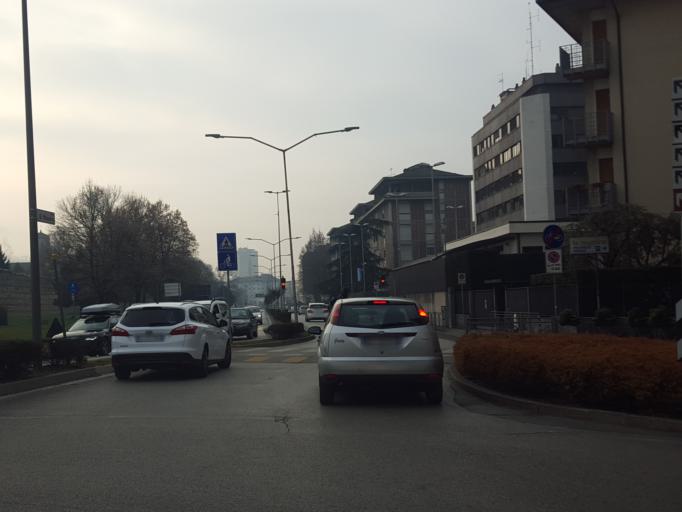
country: IT
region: Veneto
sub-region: Provincia di Vicenza
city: Vicenza
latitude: 45.5521
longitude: 11.5353
